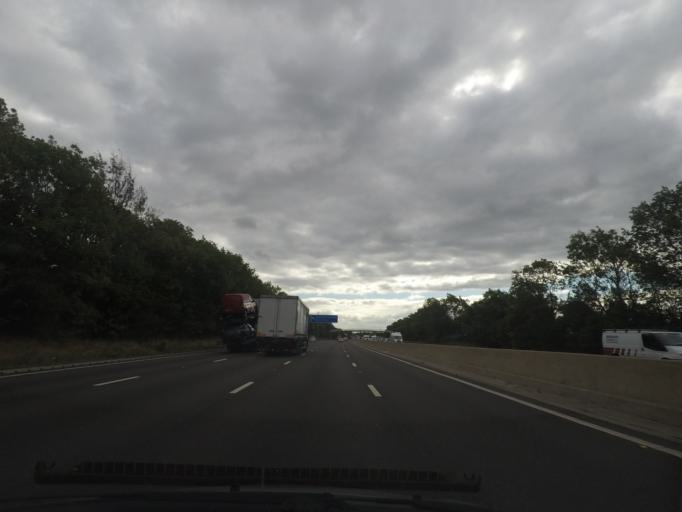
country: GB
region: England
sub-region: Derbyshire
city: Barlborough
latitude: 53.3070
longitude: -1.2851
